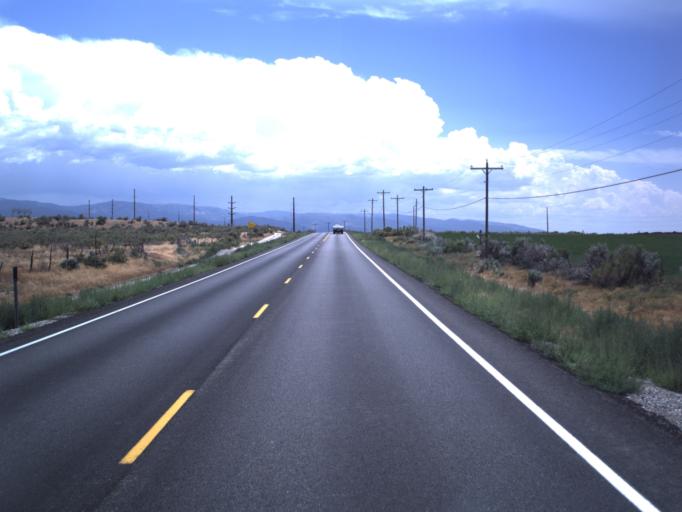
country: US
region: Utah
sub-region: Sanpete County
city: Moroni
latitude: 39.5543
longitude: -111.6003
